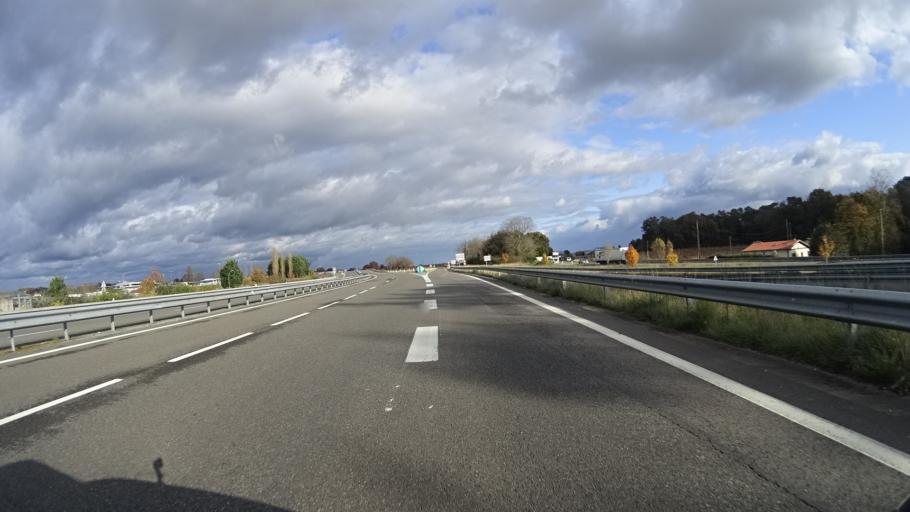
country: FR
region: Aquitaine
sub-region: Departement des Landes
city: Saint-Vincent-de-Paul
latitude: 43.7376
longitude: -1.0222
